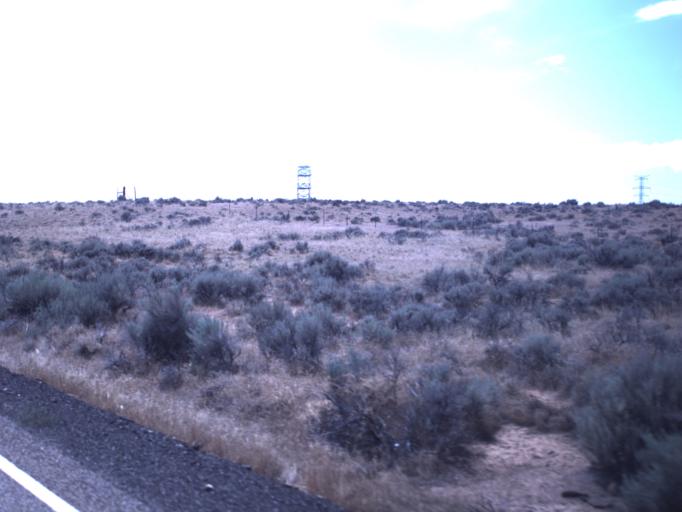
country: US
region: Utah
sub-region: Uintah County
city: Maeser
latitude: 40.2796
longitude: -109.6820
